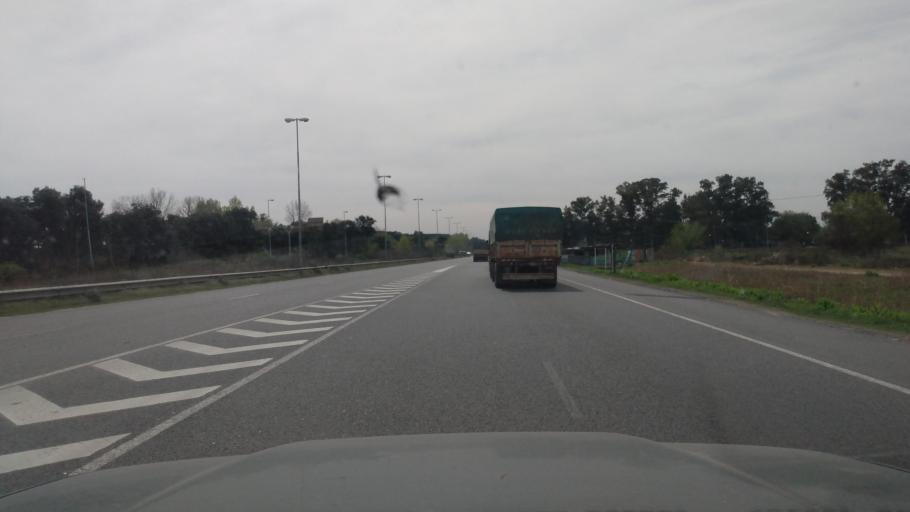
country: AR
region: Buenos Aires
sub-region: Partido de Lujan
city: Lujan
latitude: -34.4694
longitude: -59.0674
